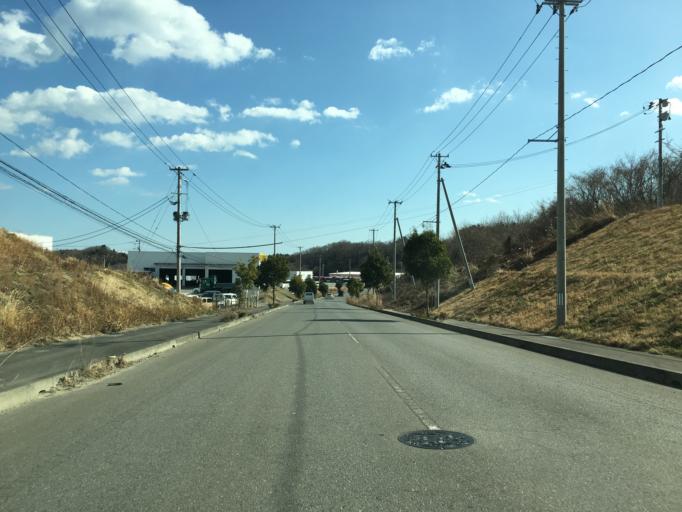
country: JP
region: Fukushima
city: Iwaki
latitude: 37.1259
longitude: 140.9735
